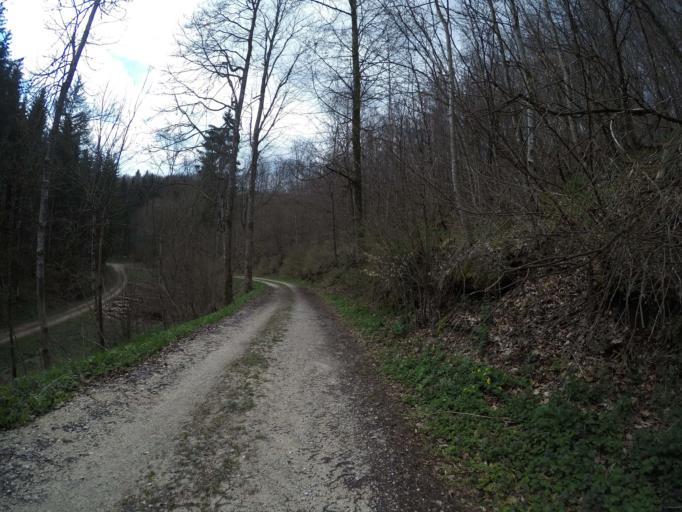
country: DE
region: Baden-Wuerttemberg
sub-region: Tuebingen Region
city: Berghulen
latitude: 48.4858
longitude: 9.8012
